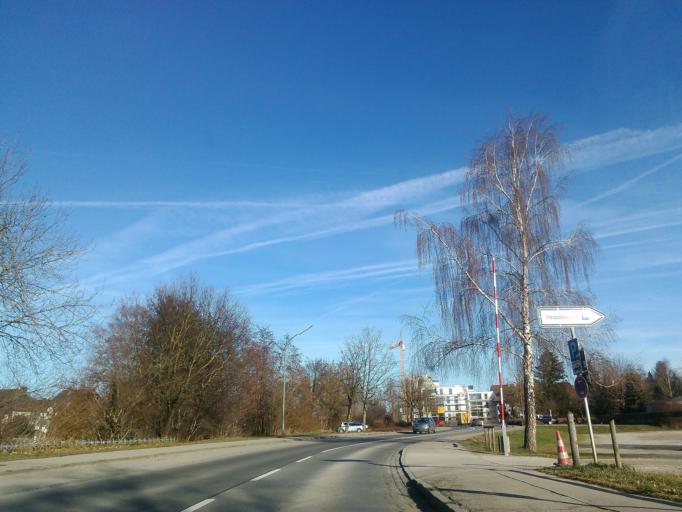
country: DE
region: Bavaria
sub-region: Swabia
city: Aichach
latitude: 48.4590
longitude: 11.1247
